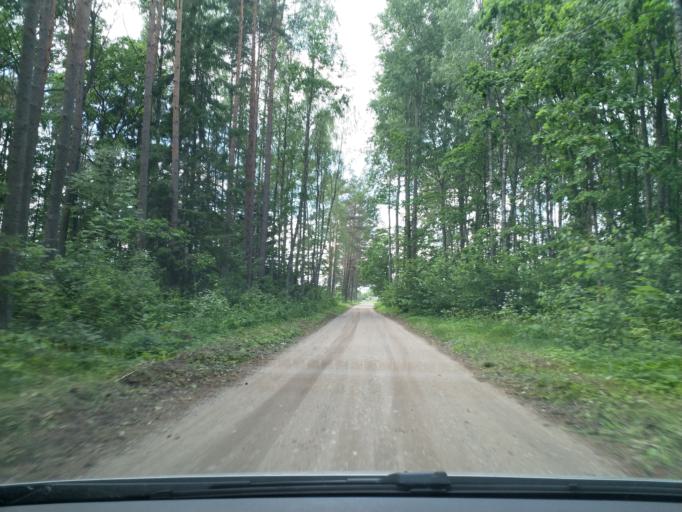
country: LV
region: Kuldigas Rajons
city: Kuldiga
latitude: 56.8382
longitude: 21.9542
